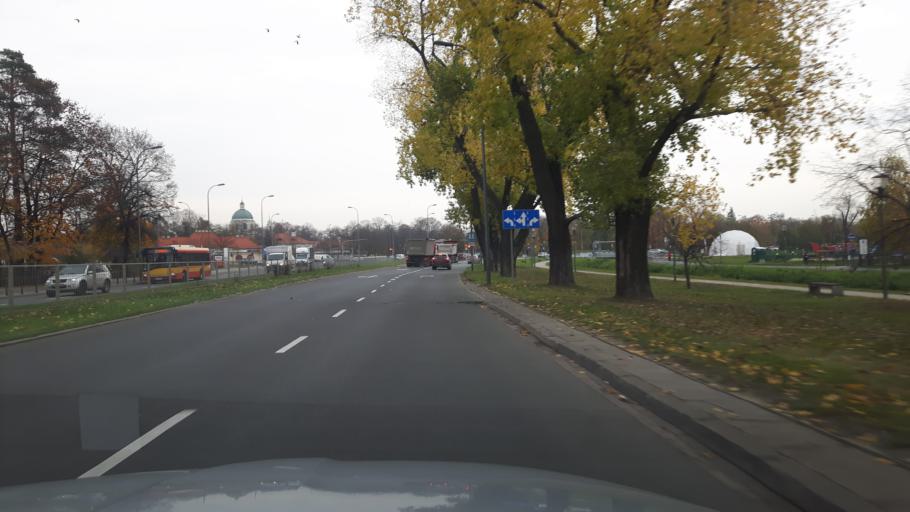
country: PL
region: Masovian Voivodeship
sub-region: Warszawa
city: Wilanow
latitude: 52.1666
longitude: 21.0815
